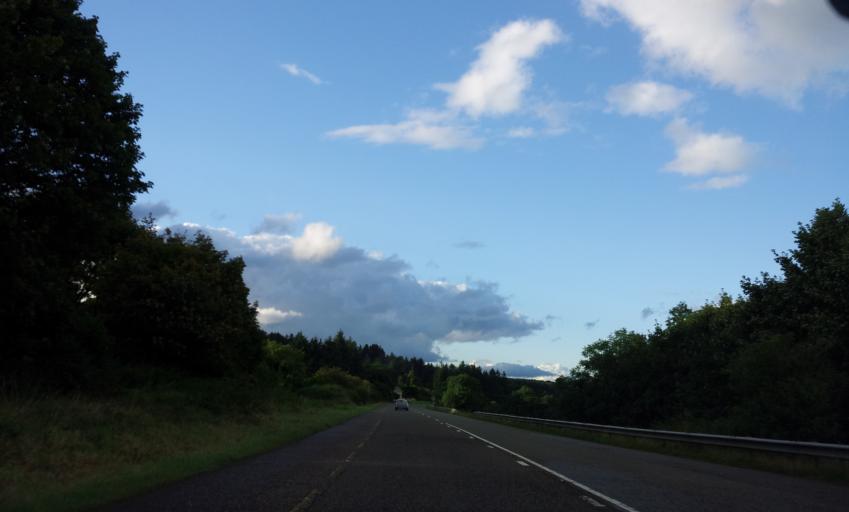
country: IE
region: Munster
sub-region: Ciarrai
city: Castleisland
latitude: 52.2819
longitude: -9.4069
